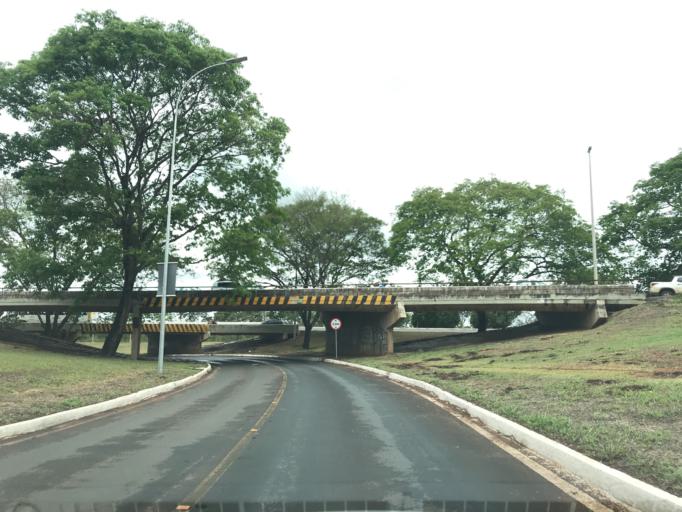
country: BR
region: Federal District
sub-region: Brasilia
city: Brasilia
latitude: -15.8026
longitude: -47.8517
